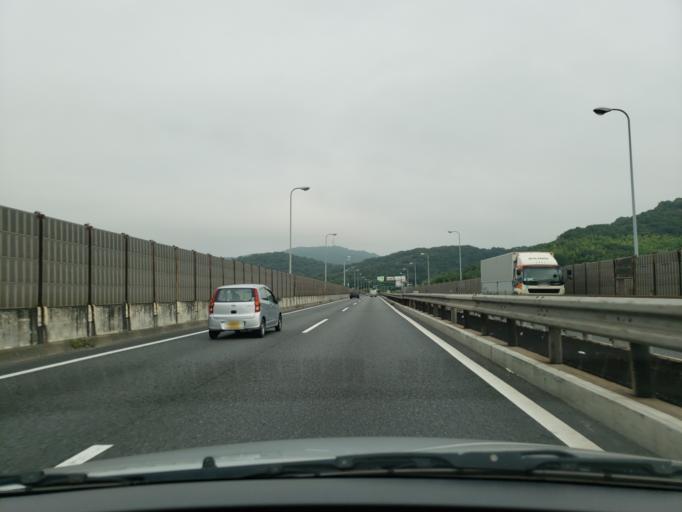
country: JP
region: Hyogo
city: Himeji
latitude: 34.8164
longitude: 134.6517
